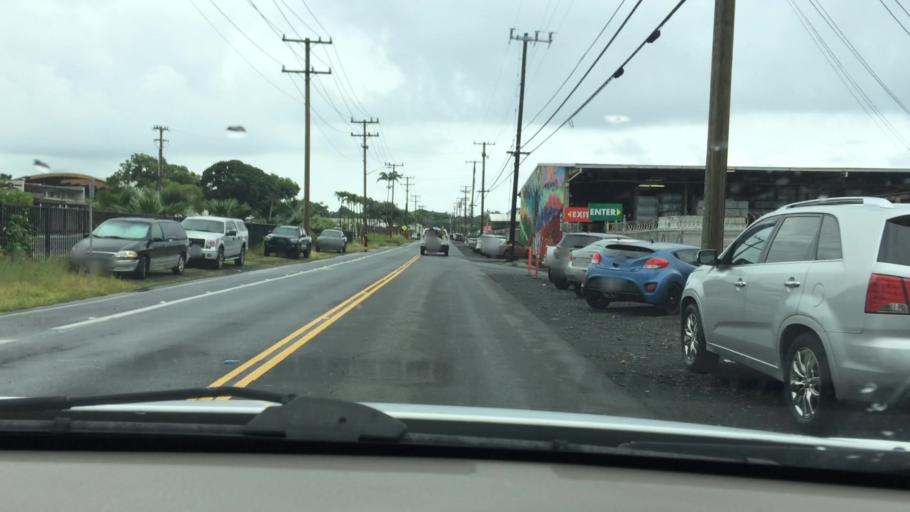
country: US
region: Hawaii
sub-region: Hawaii County
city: Hilo
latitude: 19.7171
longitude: -155.0657
